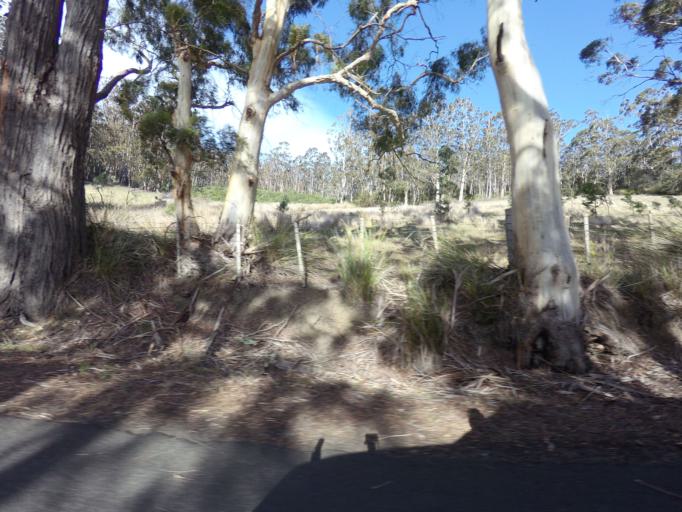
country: AU
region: Tasmania
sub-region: Kingborough
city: Kettering
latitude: -43.1645
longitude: 147.2213
